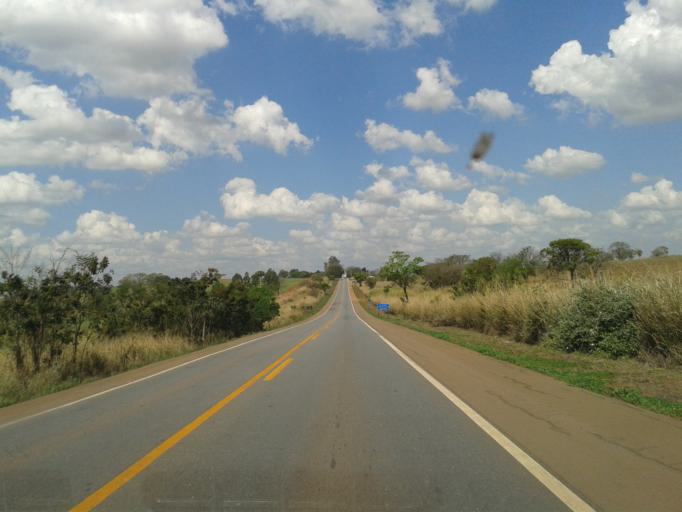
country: BR
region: Minas Gerais
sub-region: Luz
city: Luz
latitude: -19.7792
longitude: -45.7384
